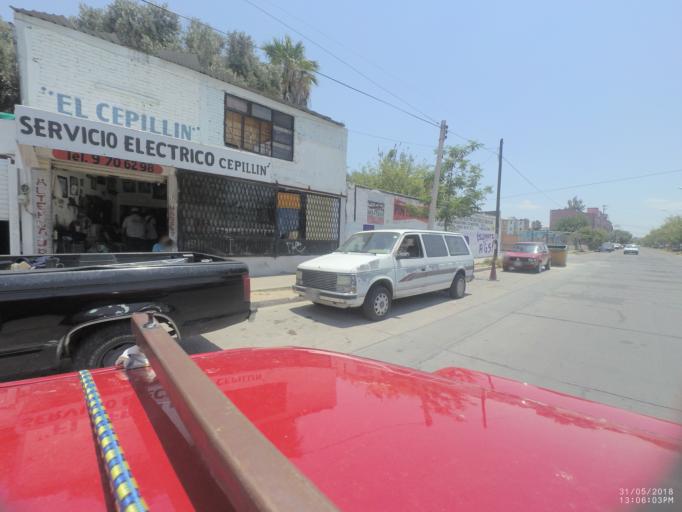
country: MX
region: Aguascalientes
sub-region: Aguascalientes
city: Aguascalientes
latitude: 21.8737
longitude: -102.2860
